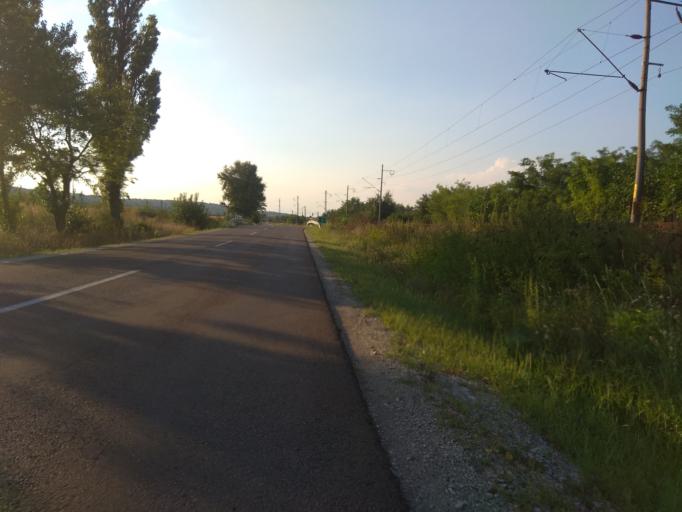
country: HU
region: Borsod-Abauj-Zemplen
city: Nyekladhaza
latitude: 47.9832
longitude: 20.8420
